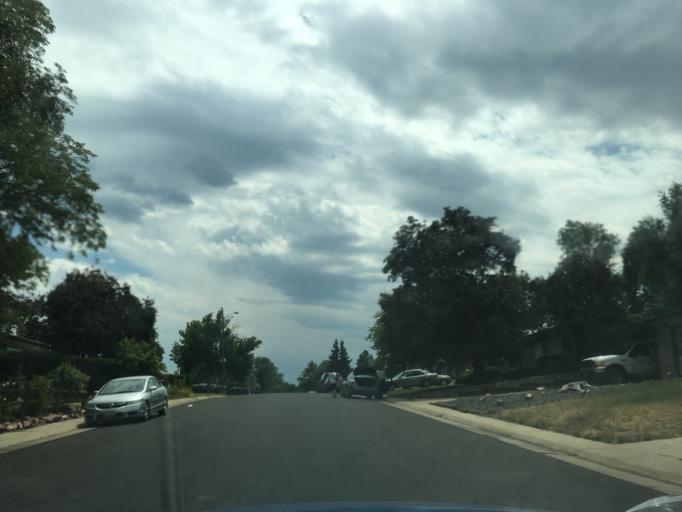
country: US
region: Colorado
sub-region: Jefferson County
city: Lakewood
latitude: 39.6820
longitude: -105.0522
